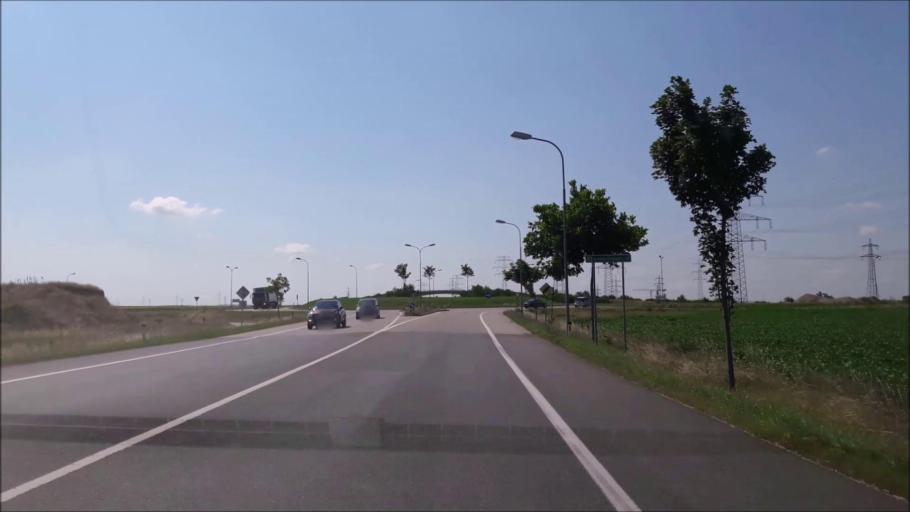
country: AT
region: Lower Austria
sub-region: Politischer Bezirk Wien-Umgebung
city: Himberg
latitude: 48.0841
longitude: 16.4577
